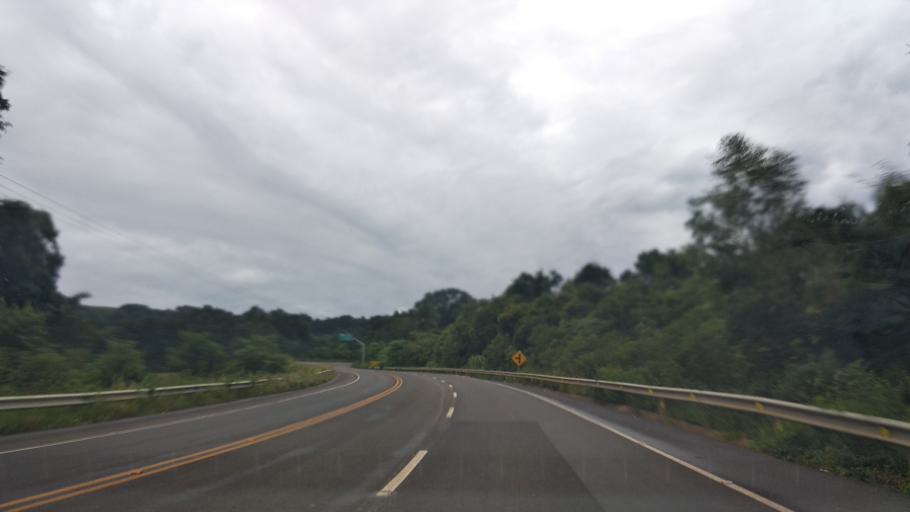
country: BR
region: Santa Catarina
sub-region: Videira
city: Videira
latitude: -27.0747
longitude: -51.2347
